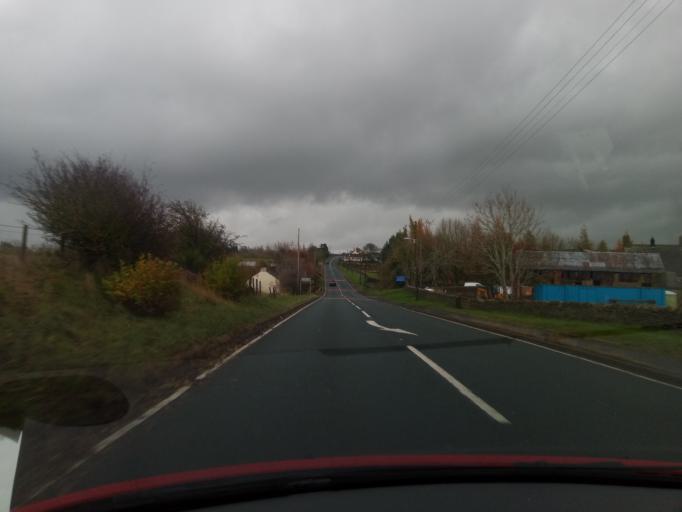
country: GB
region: England
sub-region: County Durham
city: Castleside
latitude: 54.8271
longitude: -1.8656
